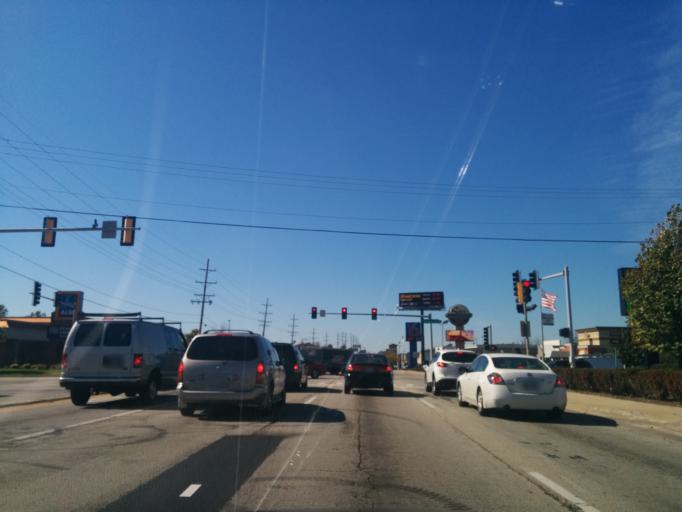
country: US
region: Illinois
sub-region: DuPage County
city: Oakbrook Terrace
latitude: 41.8605
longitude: -87.9774
